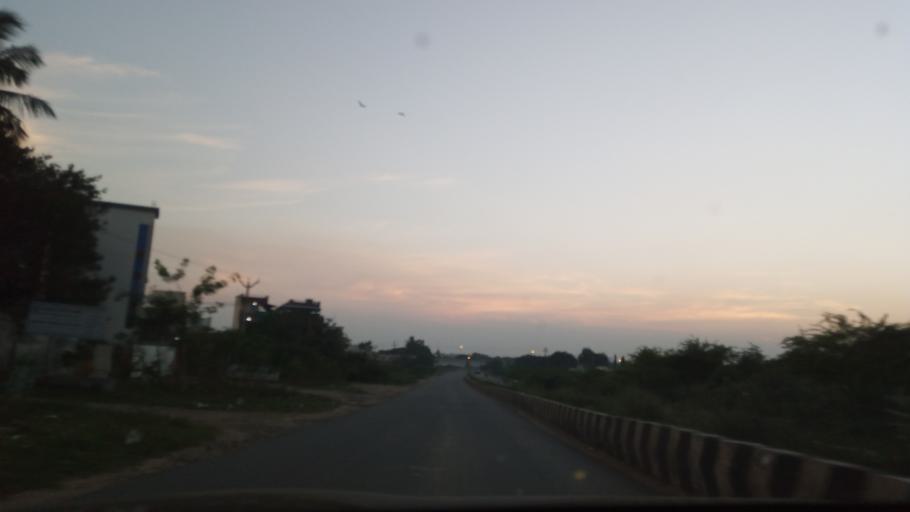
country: IN
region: Tamil Nadu
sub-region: Vellore
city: Walajapet
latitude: 12.9236
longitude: 79.3451
